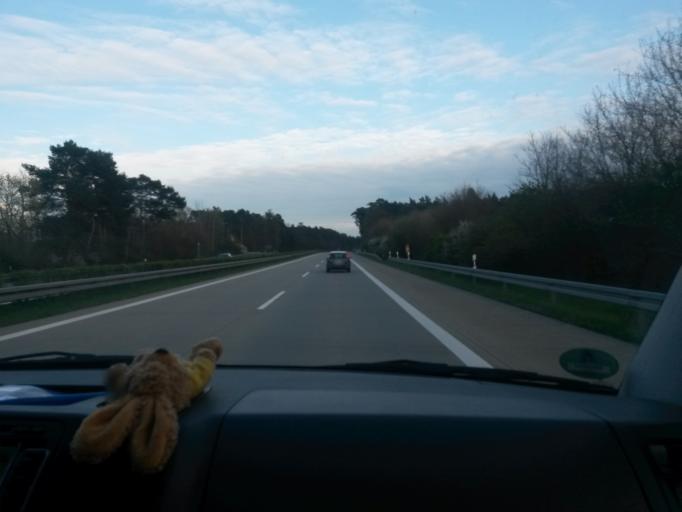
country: DE
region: Brandenburg
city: Lubbenau
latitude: 51.8279
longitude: 13.9964
